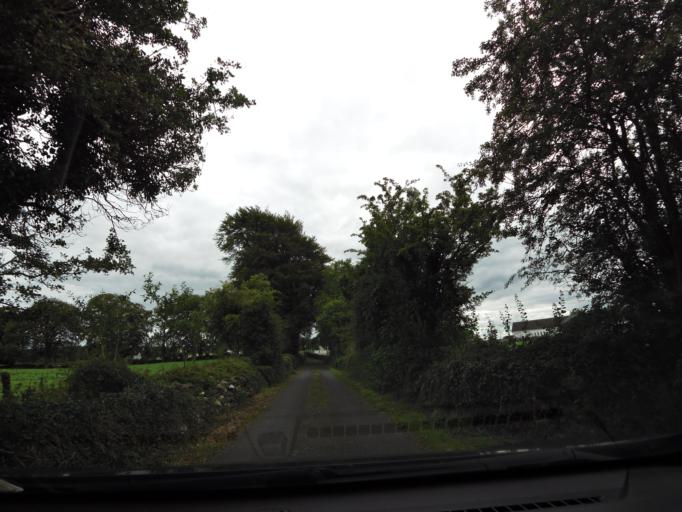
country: IE
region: Connaught
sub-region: County Galway
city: Loughrea
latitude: 53.1489
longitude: -8.4169
